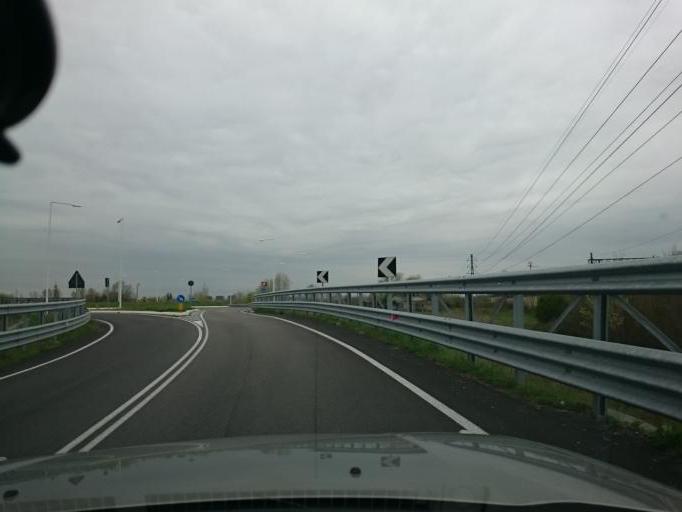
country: IT
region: Veneto
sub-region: Provincia di Padova
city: Cadoneghe
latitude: 45.4238
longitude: 11.9213
